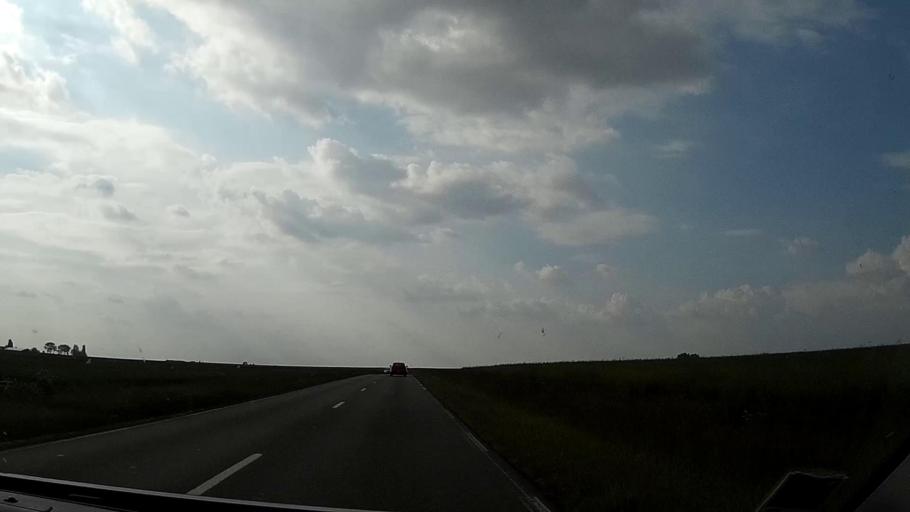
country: FR
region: Centre
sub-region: Departement du Loir-et-Cher
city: Herbault
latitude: 47.7054
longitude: 1.1719
